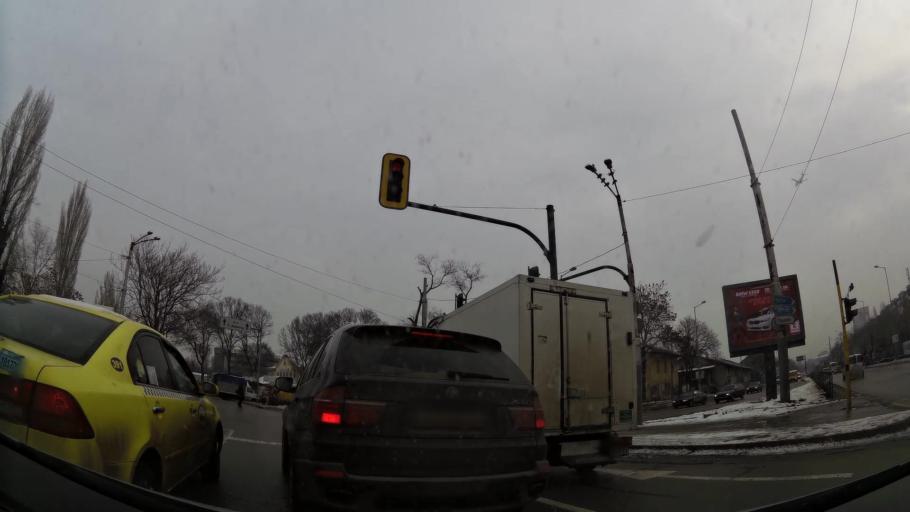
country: BG
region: Sofia-Capital
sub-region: Stolichna Obshtina
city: Sofia
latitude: 42.7049
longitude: 23.3335
